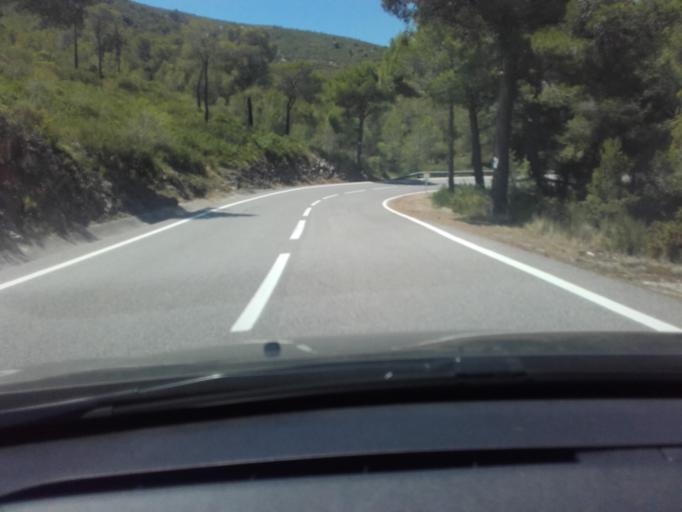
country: ES
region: Catalonia
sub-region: Provincia de Tarragona
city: la Bisbal del Penedes
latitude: 41.3060
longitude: 1.4662
